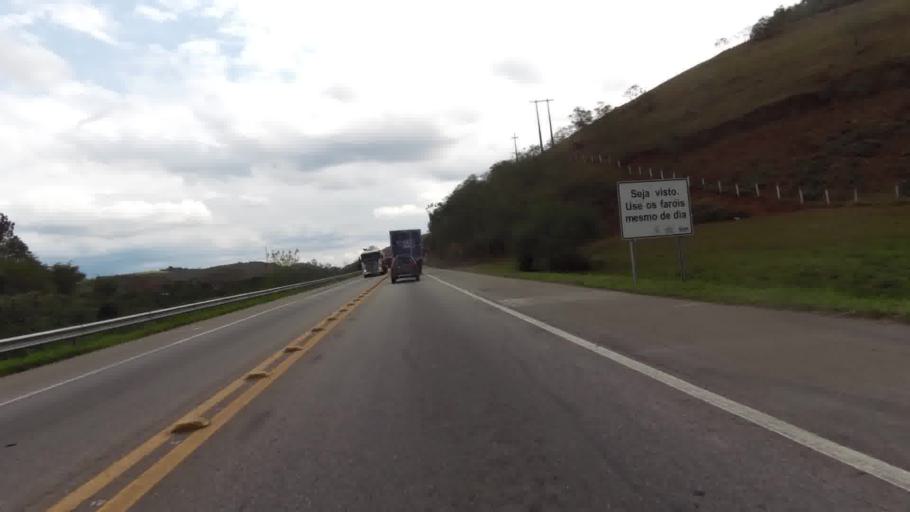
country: BR
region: Rio de Janeiro
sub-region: Rio Das Ostras
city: Rio das Ostras
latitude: -22.4623
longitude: -42.0649
